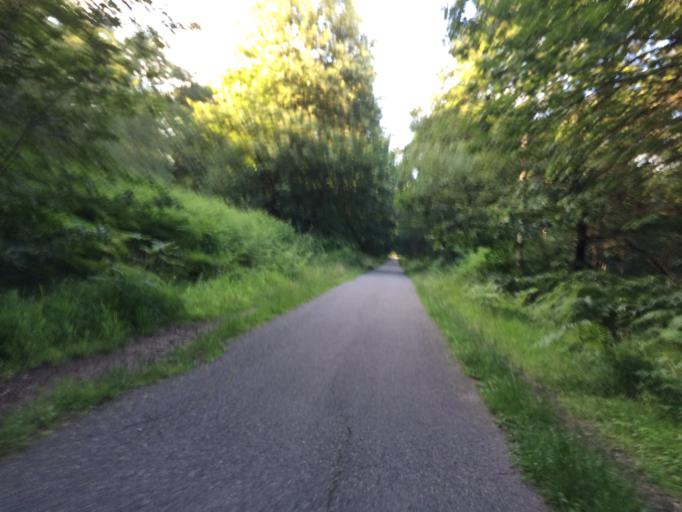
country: FR
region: Ile-de-France
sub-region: Departement de l'Essonne
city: Montgeron
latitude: 48.6822
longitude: 2.4653
